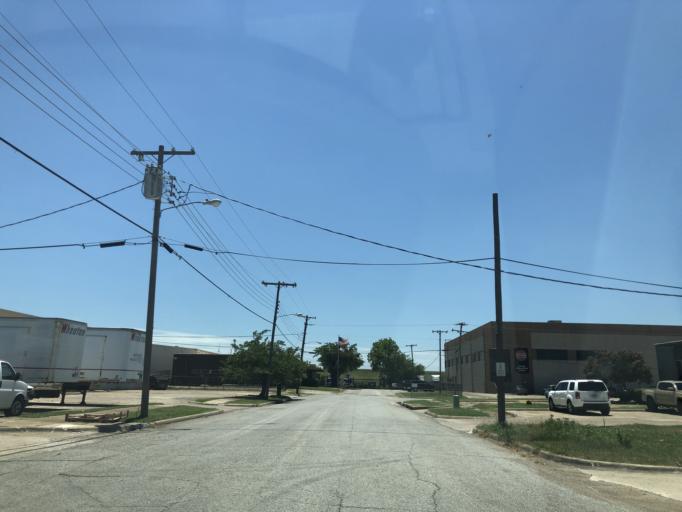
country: US
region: Texas
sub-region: Dallas County
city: Irving
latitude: 32.8046
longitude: -96.8824
